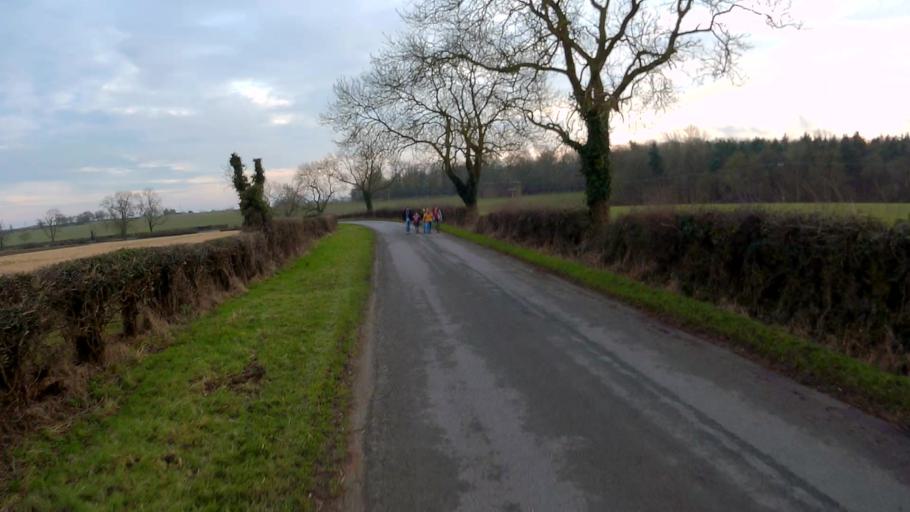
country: GB
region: England
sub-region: Lincolnshire
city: Bourne
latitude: 52.8324
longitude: -0.4468
